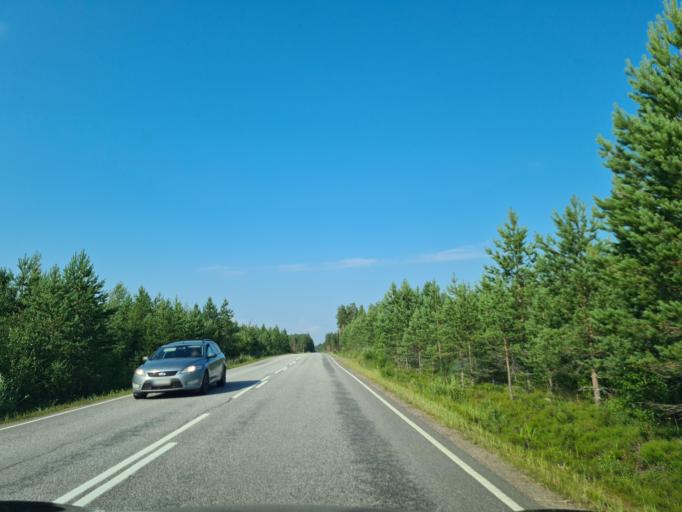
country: FI
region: Satakunta
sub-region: Pohjois-Satakunta
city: Karvia
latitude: 62.2951
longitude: 22.6232
